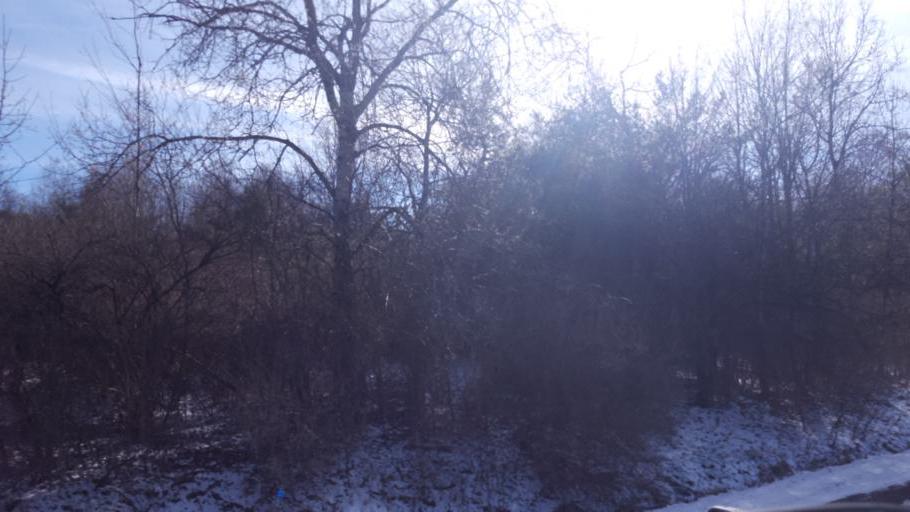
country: US
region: New York
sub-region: Allegany County
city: Wellsville
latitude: 42.1219
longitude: -77.9825
